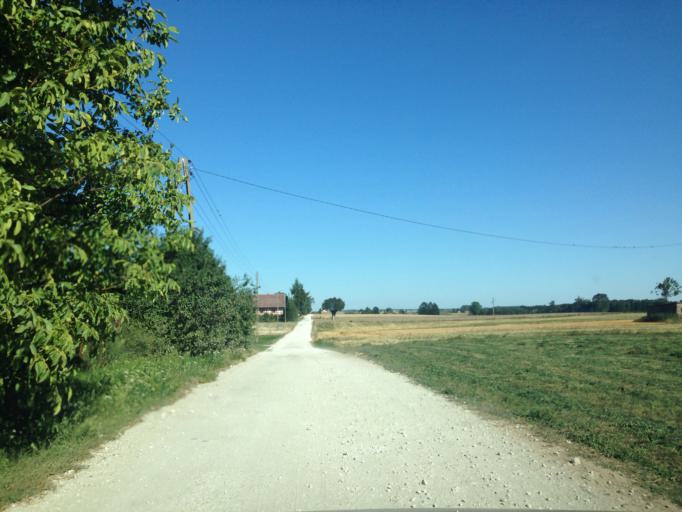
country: PL
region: Kujawsko-Pomorskie
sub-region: Powiat brodnicki
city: Swiedziebnia
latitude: 53.1903
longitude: 19.5641
